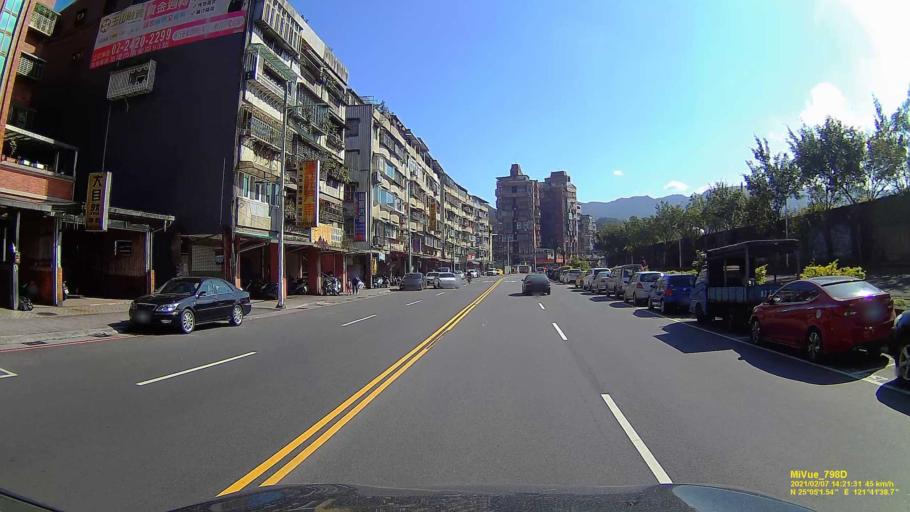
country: TW
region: Taiwan
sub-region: Keelung
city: Keelung
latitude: 25.0835
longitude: 121.6941
